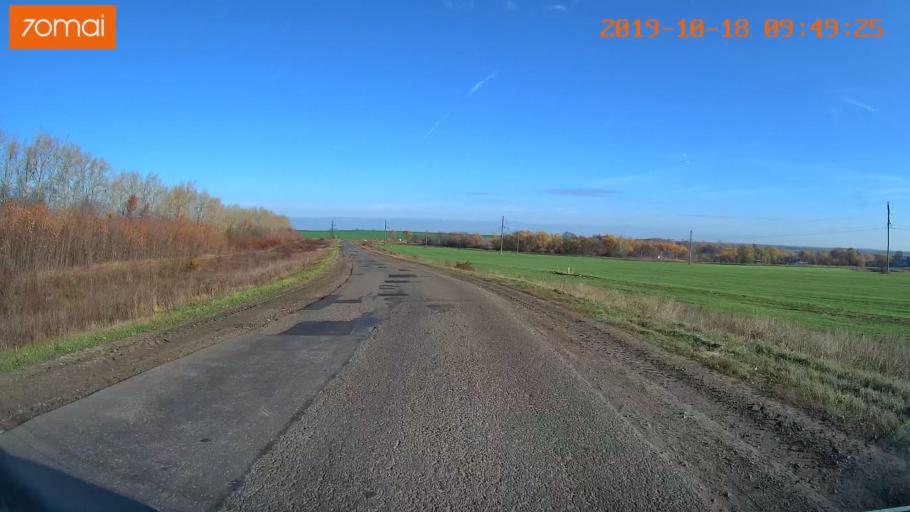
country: RU
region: Tula
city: Kazachka
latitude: 53.3177
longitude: 38.2678
